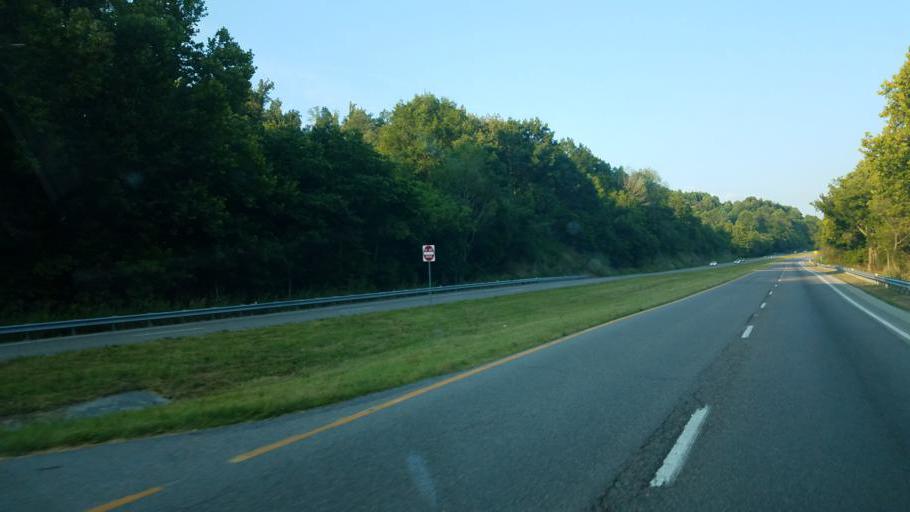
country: US
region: Tennessee
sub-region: Hawkins County
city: Mount Carmel
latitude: 36.6413
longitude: -82.7058
